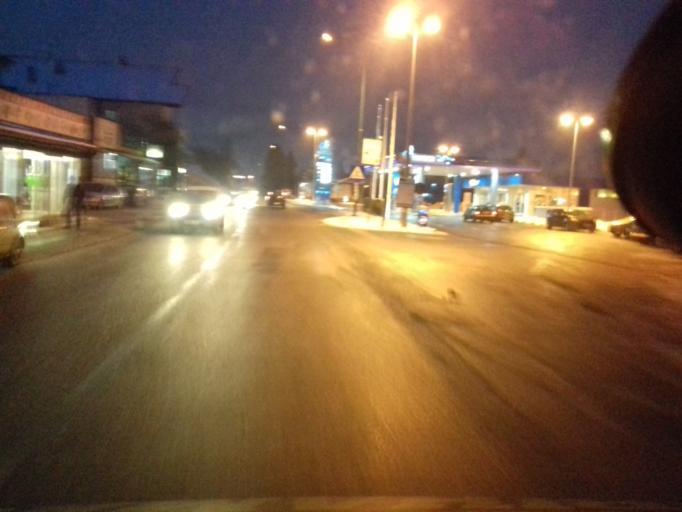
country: BA
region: Federation of Bosnia and Herzegovina
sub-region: Kanton Sarajevo
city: Sarajevo
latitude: 43.8575
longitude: 18.3222
